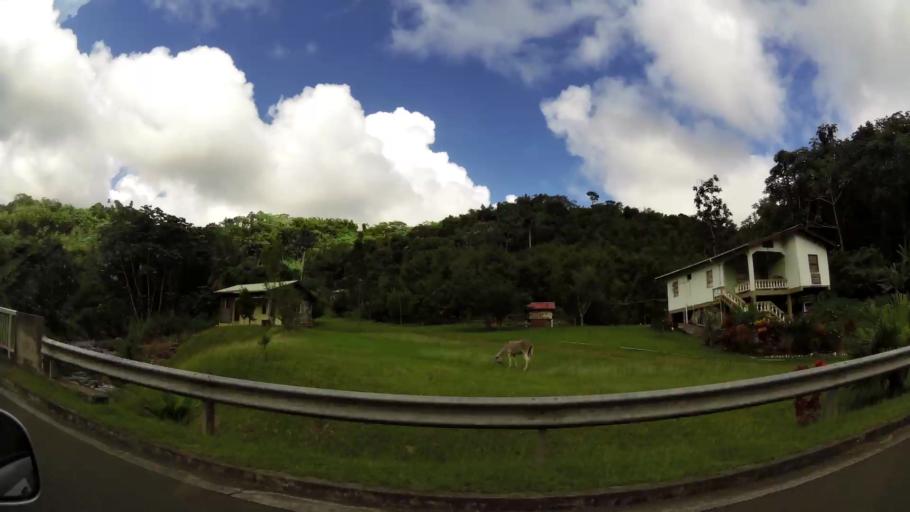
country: GD
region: Saint Andrew
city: Grenville
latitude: 12.1280
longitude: -61.6556
